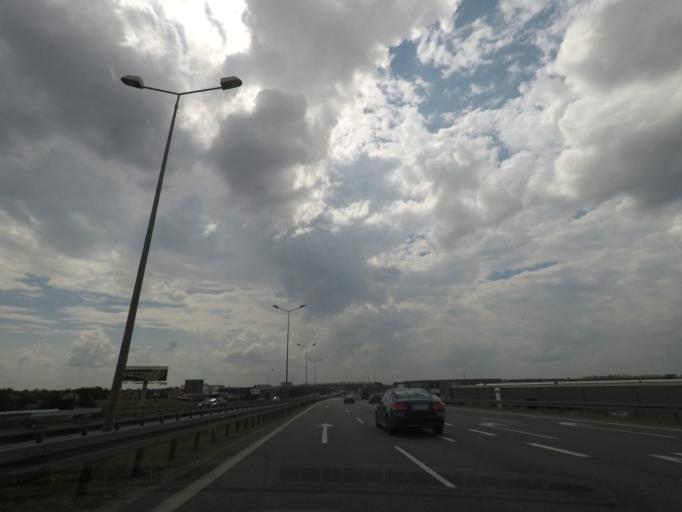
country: PL
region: Masovian Voivodeship
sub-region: Powiat pruszkowski
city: Piastow
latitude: 52.2062
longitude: 20.8499
